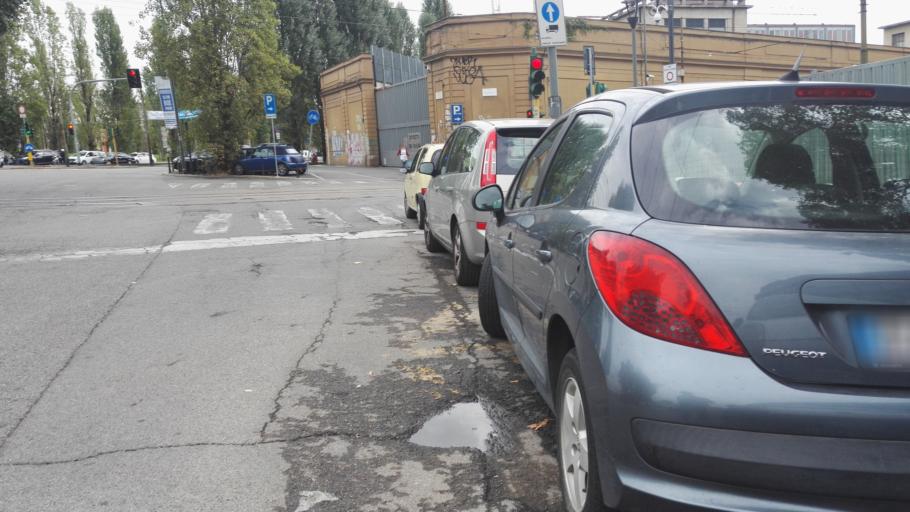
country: IT
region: Lombardy
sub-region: Citta metropolitana di Milano
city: Milano
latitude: 45.4840
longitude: 9.1771
